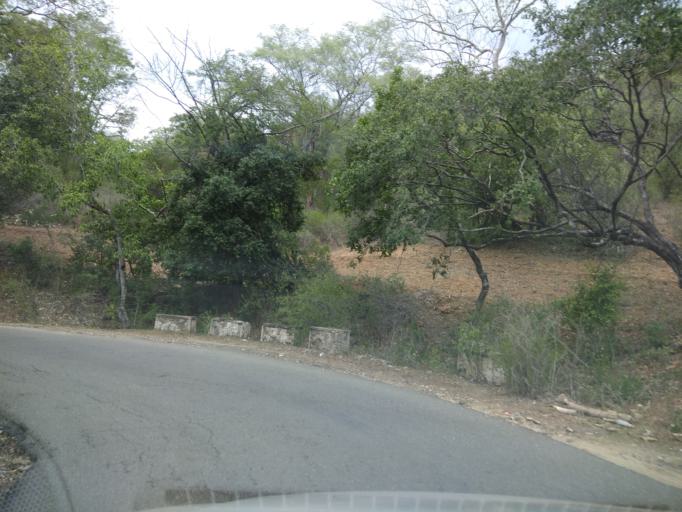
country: IN
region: Tamil Nadu
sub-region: Tiruppur
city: Dhali
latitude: 10.3374
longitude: 77.2174
